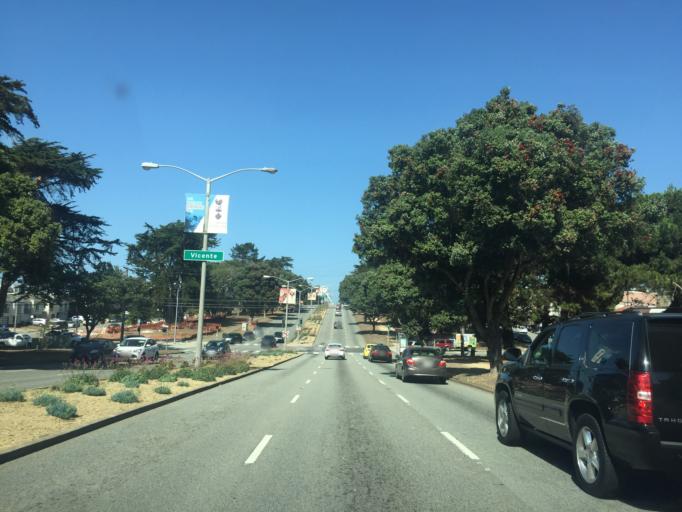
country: US
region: California
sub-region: San Mateo County
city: Daly City
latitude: 37.7377
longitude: -122.4941
